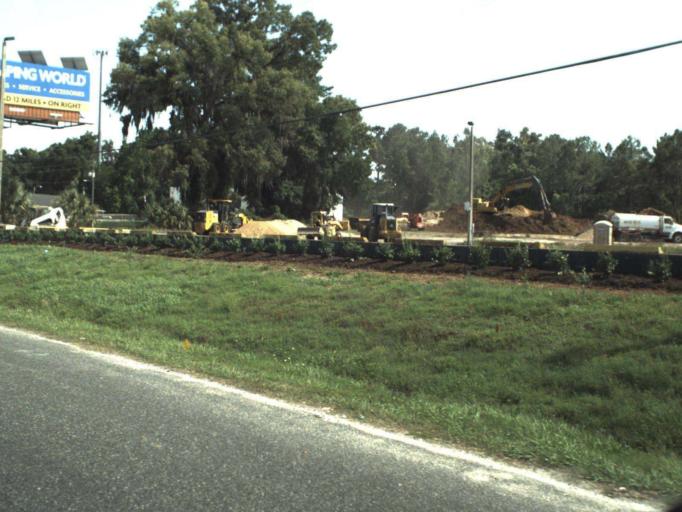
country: US
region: Florida
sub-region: Marion County
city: Ocala
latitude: 29.1520
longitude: -82.1225
